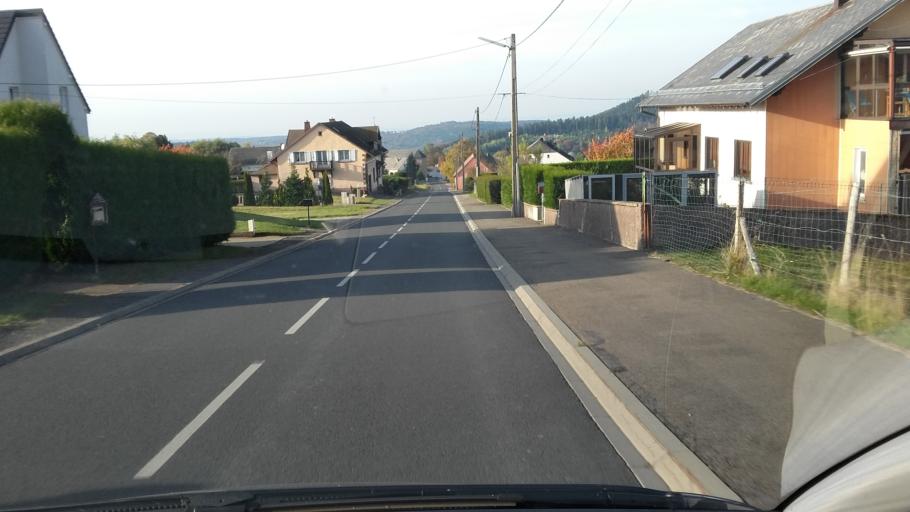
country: FR
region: Lorraine
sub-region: Departement de la Moselle
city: Dabo
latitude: 48.6509
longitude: 7.2732
